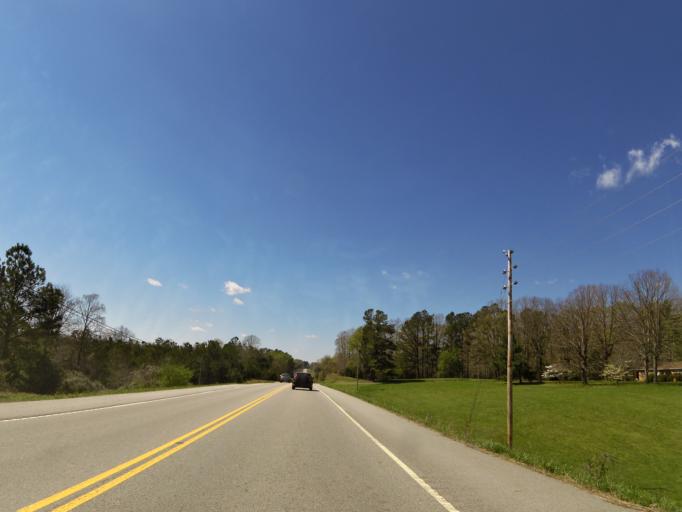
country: US
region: Tennessee
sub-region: DeKalb County
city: Smithville
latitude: 35.9641
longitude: -85.6387
